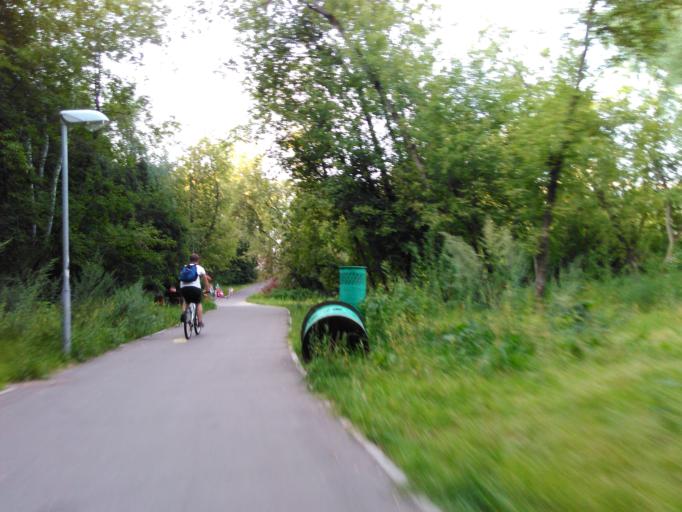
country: RU
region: Moscow
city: Vorob'yovo
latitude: 55.7299
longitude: 37.5351
